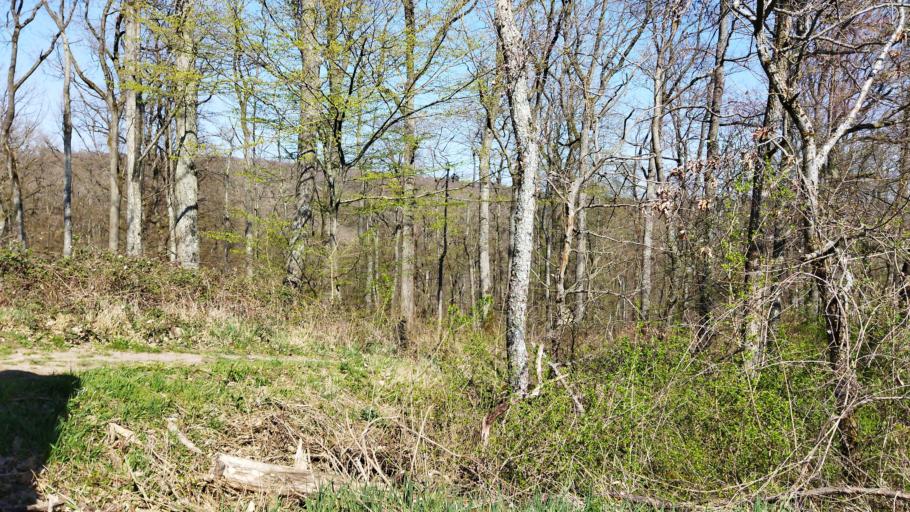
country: DE
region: Baden-Wuerttemberg
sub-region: Karlsruhe Region
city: Sternenfels
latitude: 49.0234
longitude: 8.8737
